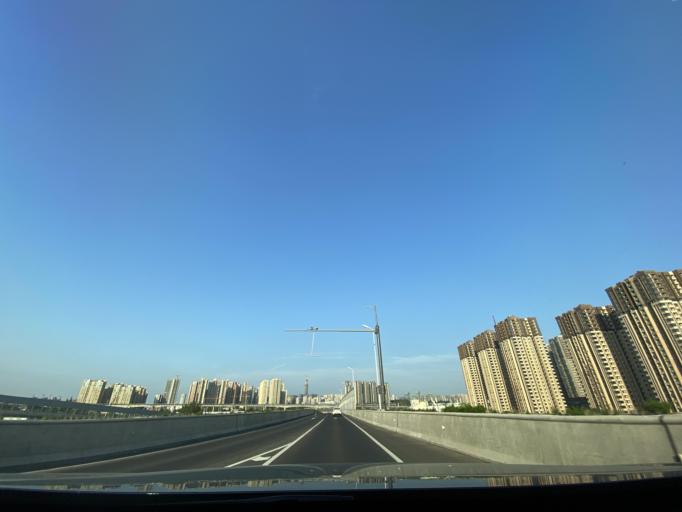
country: CN
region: Sichuan
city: Chengdu
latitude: 30.5981
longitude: 104.1071
